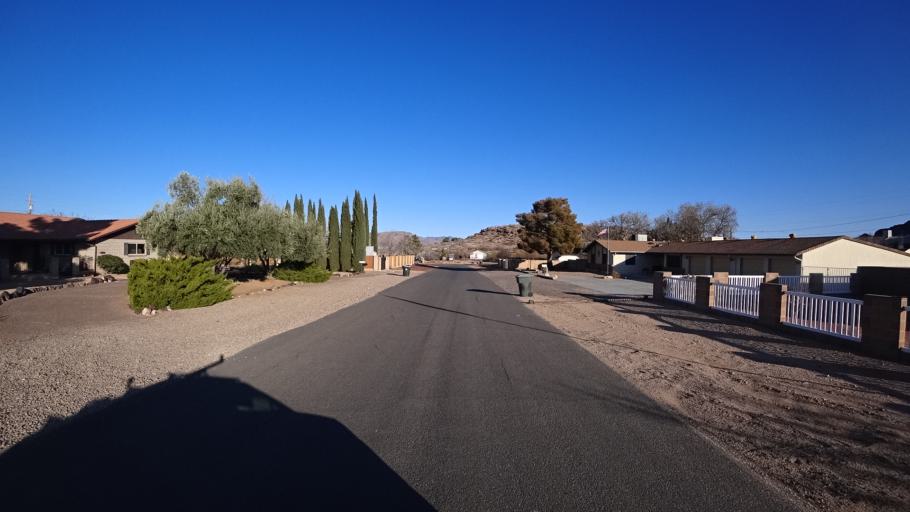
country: US
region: Arizona
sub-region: Mohave County
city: Kingman
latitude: 35.2061
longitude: -114.0076
